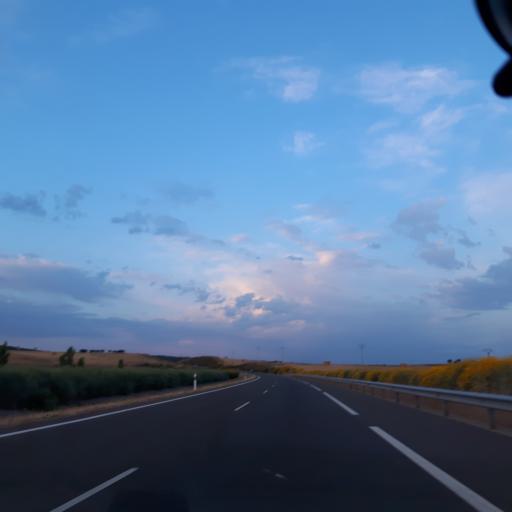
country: ES
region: Castille and Leon
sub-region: Provincia de Salamanca
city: Mozarbez
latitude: 40.8506
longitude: -5.6415
